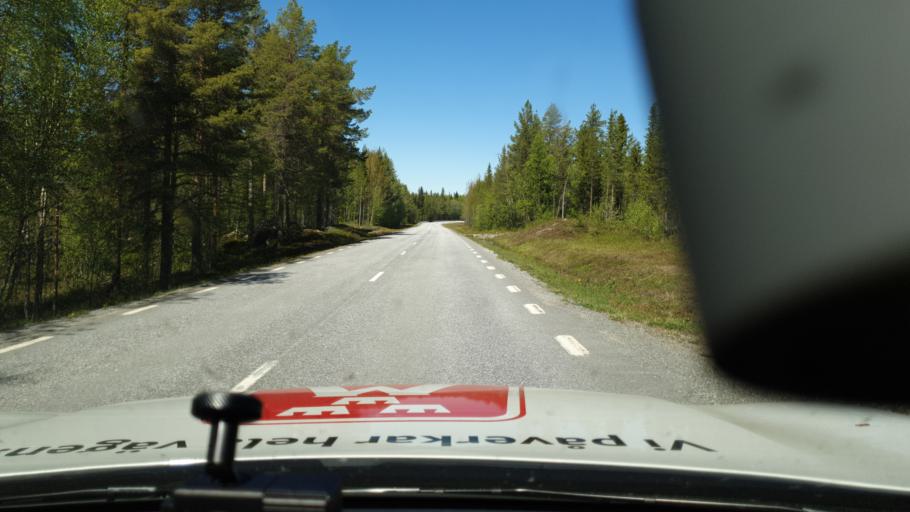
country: SE
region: Vaesterbotten
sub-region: Storumans Kommun
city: Storuman
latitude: 65.1760
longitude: 17.0231
